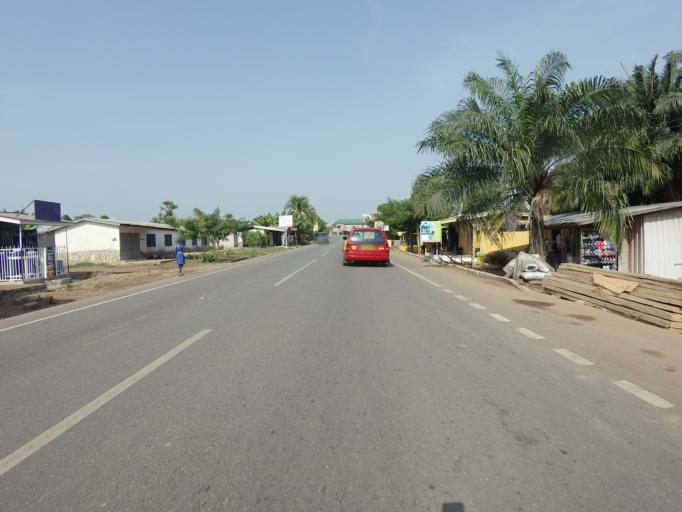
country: GH
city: Akropong
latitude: 6.1157
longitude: -0.0046
